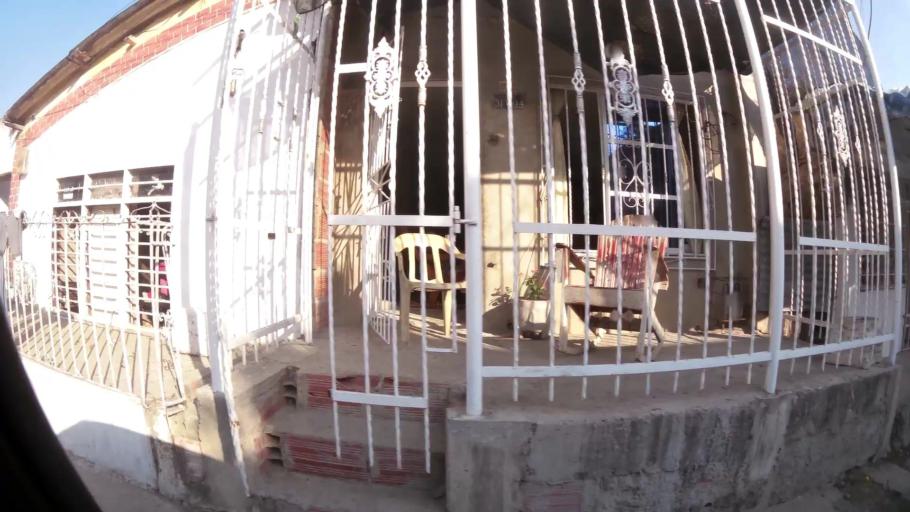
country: CO
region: Bolivar
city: Cartagena
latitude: 10.4086
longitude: -75.4956
